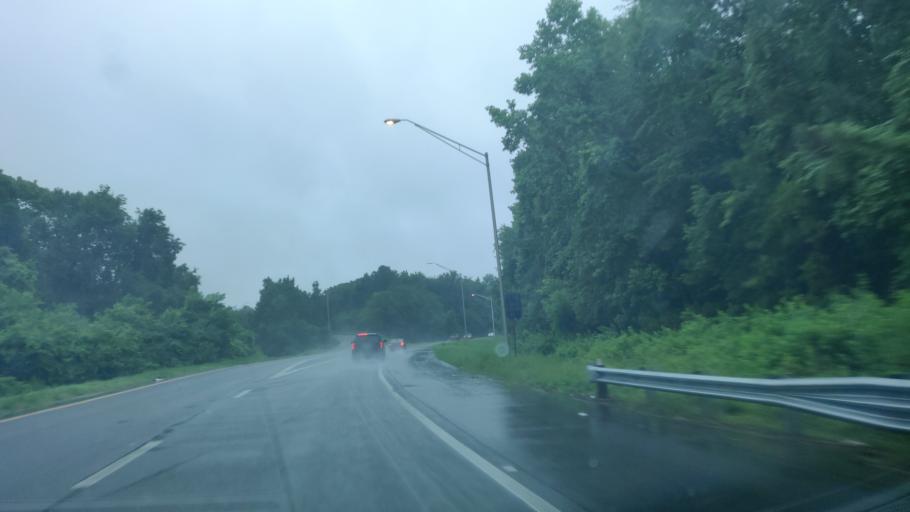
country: US
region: Florida
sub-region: Duval County
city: Jacksonville
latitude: 30.3144
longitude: -81.7735
